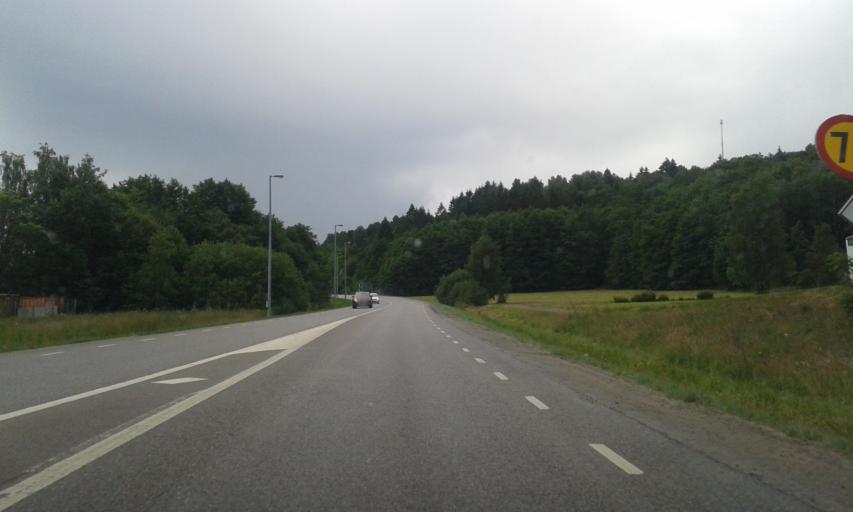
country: SE
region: Vaestra Goetaland
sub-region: Kungalvs Kommun
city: Kungalv
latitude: 57.8869
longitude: 11.9858
